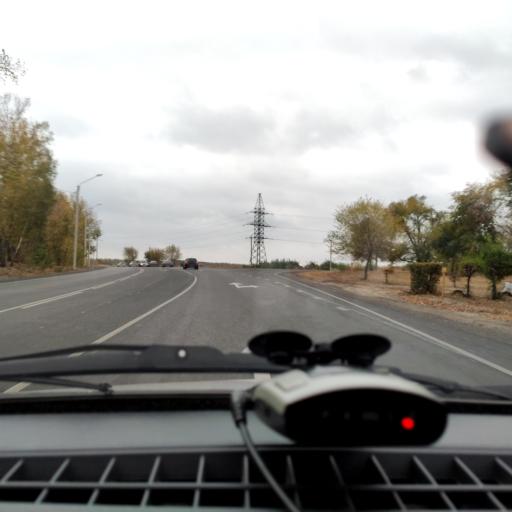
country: RU
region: Voronezj
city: Pridonskoy
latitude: 51.7003
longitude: 39.0787
